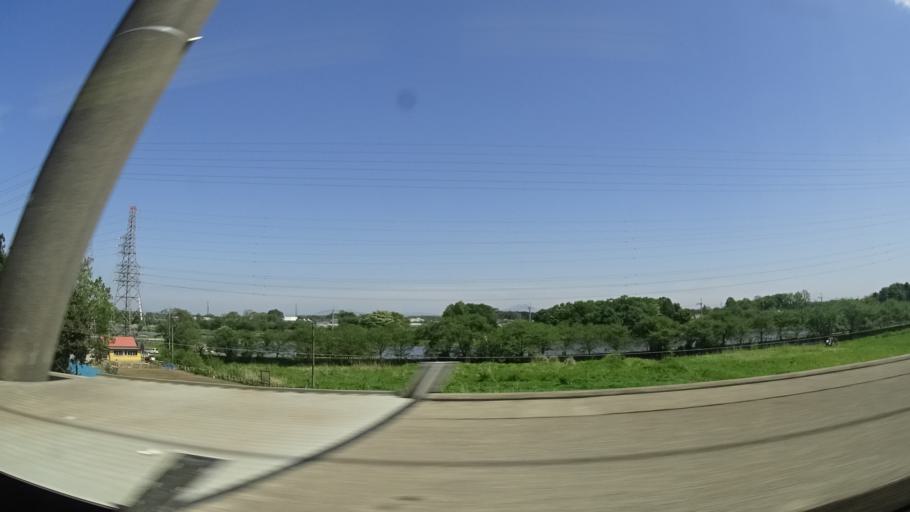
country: JP
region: Tochigi
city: Oyama
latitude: 36.3517
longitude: 139.8289
